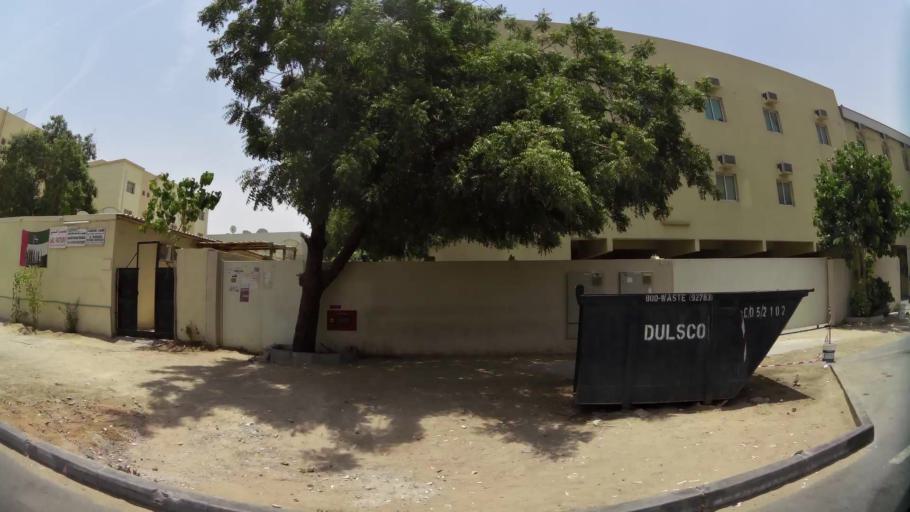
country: AE
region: Ash Shariqah
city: Sharjah
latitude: 25.2668
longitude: 55.4298
